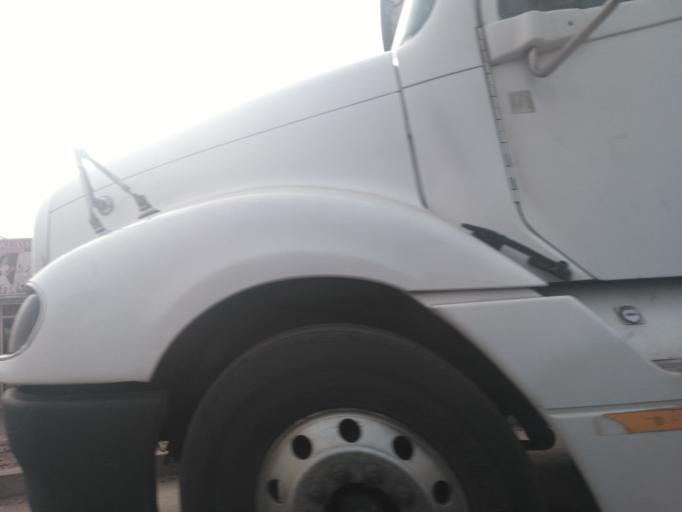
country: GH
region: Ashanti
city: Kumasi
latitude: 6.6823
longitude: -1.6443
